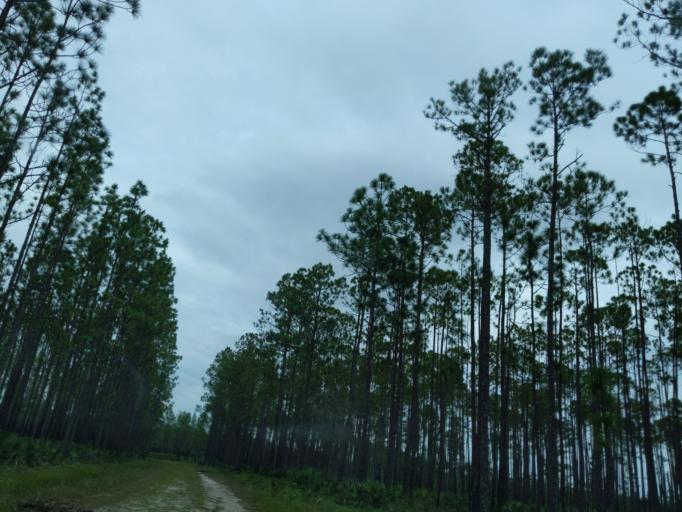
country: US
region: Florida
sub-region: Gadsden County
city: Midway
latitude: 30.3507
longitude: -84.4906
